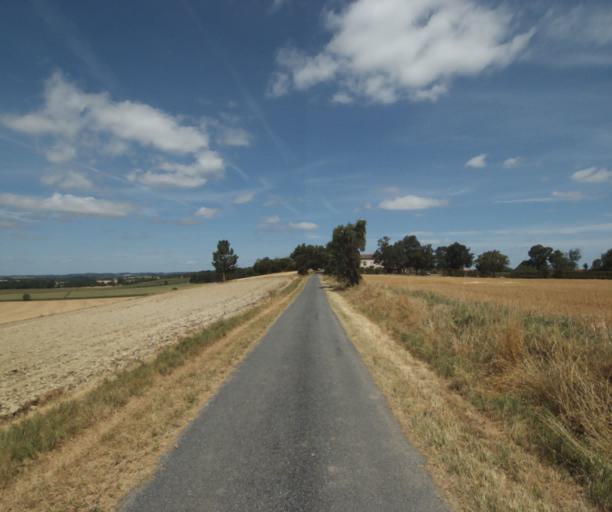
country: FR
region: Midi-Pyrenees
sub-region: Departement du Tarn
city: Dourgne
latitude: 43.4985
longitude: 2.0967
